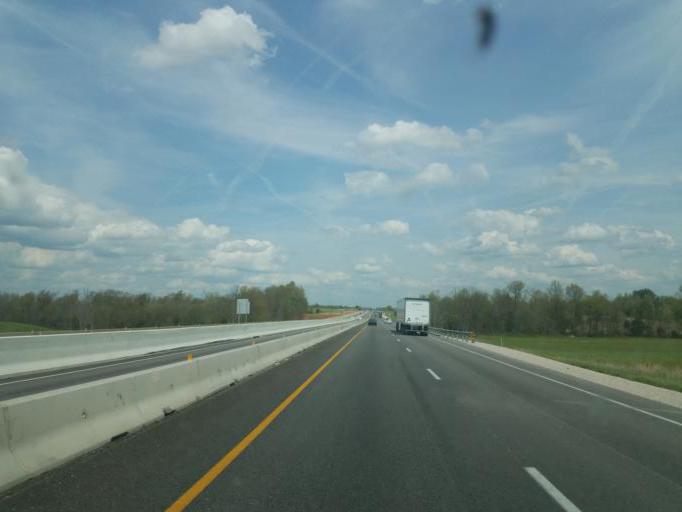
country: US
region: Kentucky
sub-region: Larue County
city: Hodgenville
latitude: 37.5403
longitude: -85.8807
